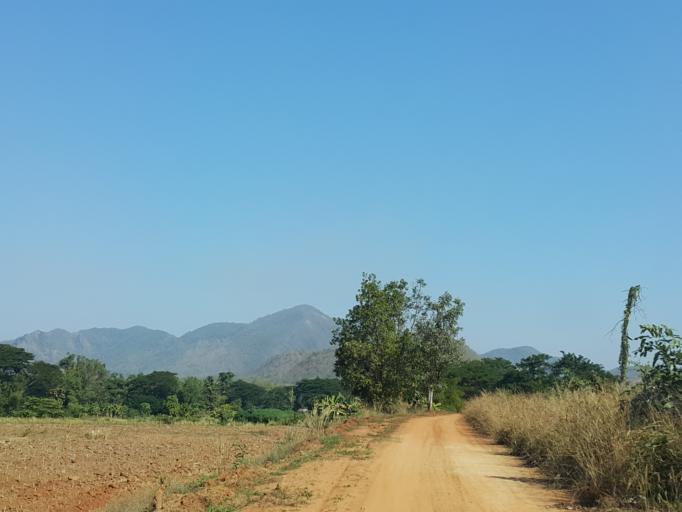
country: TH
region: Sukhothai
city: Thung Saliam
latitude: 17.3189
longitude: 99.4520
